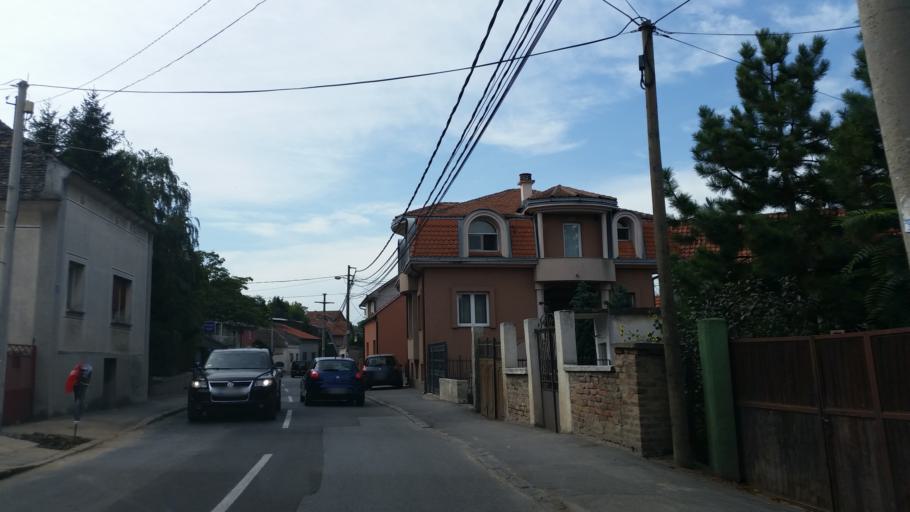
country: RS
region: Central Serbia
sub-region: Belgrade
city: Palilula
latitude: 44.8298
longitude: 20.5466
